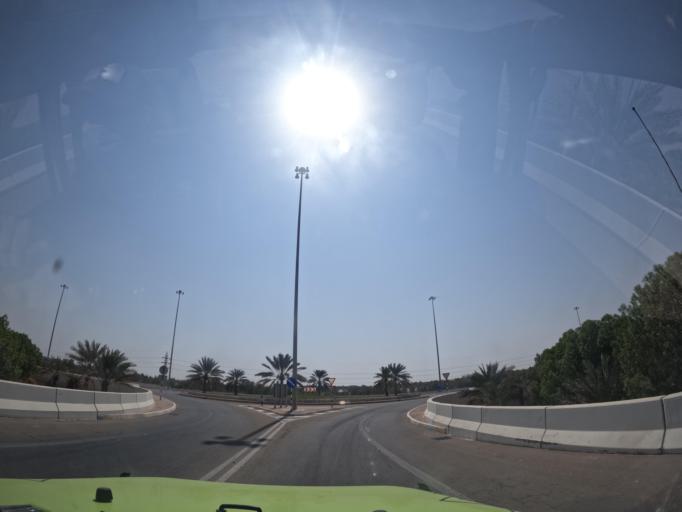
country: AE
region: Abu Dhabi
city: Al Ain
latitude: 24.1754
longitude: 55.1359
